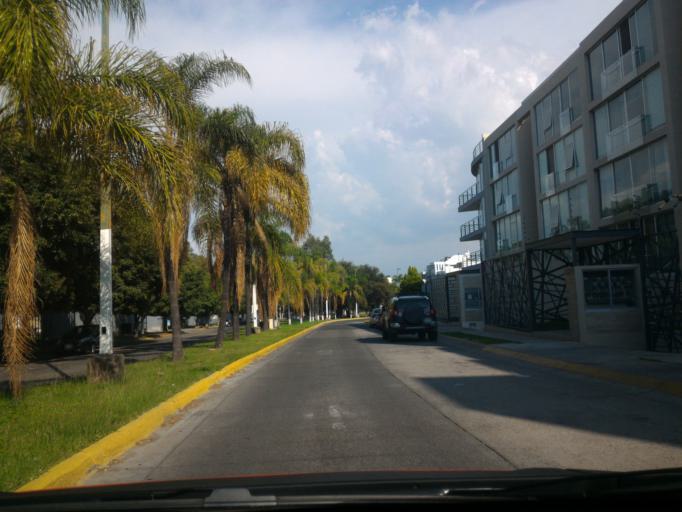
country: MX
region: Jalisco
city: Guadalajara
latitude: 20.6641
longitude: -103.4465
